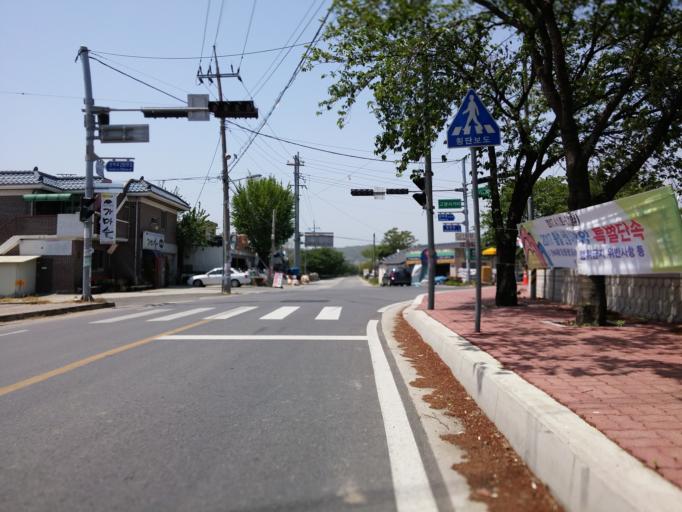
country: KR
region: Chungcheongnam-do
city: Nonsan
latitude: 36.2145
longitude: 127.1974
